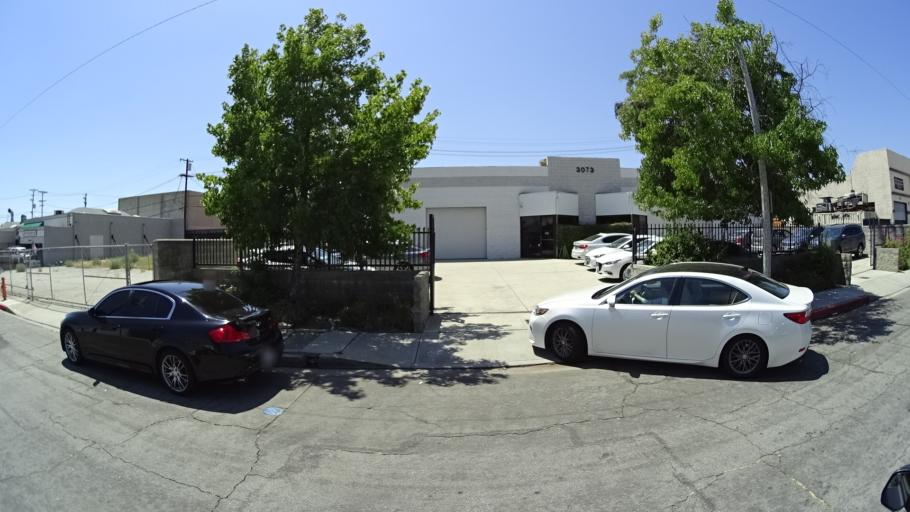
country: US
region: California
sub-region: Los Angeles County
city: Burbank
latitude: 34.2054
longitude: -118.3455
